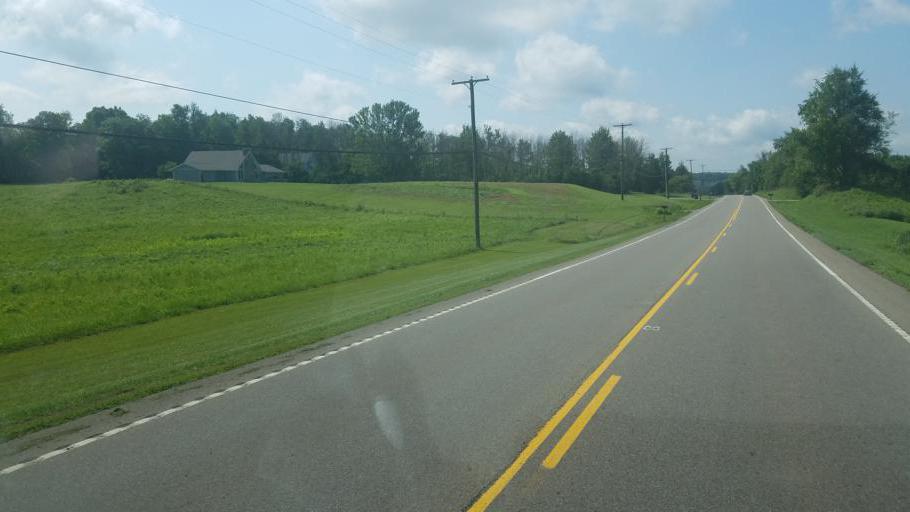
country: US
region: Ohio
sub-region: Licking County
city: Granville South
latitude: 40.0337
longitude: -82.5233
